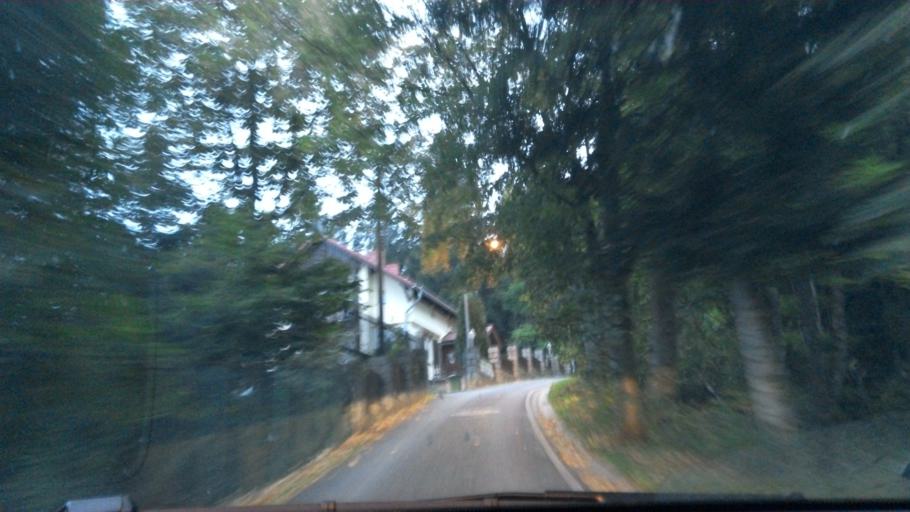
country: PL
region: Lower Silesian Voivodeship
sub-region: Powiat jeleniogorski
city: Karpacz
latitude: 50.7682
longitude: 15.7505
